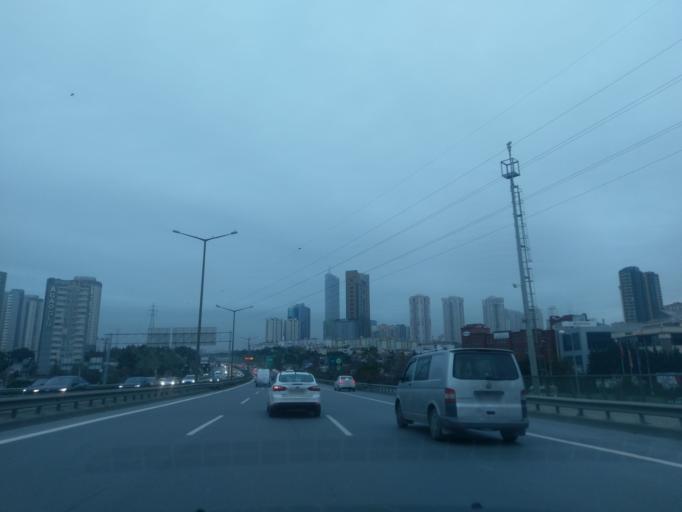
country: TR
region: Istanbul
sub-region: Atasehir
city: Atasehir
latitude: 40.9854
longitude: 29.1053
